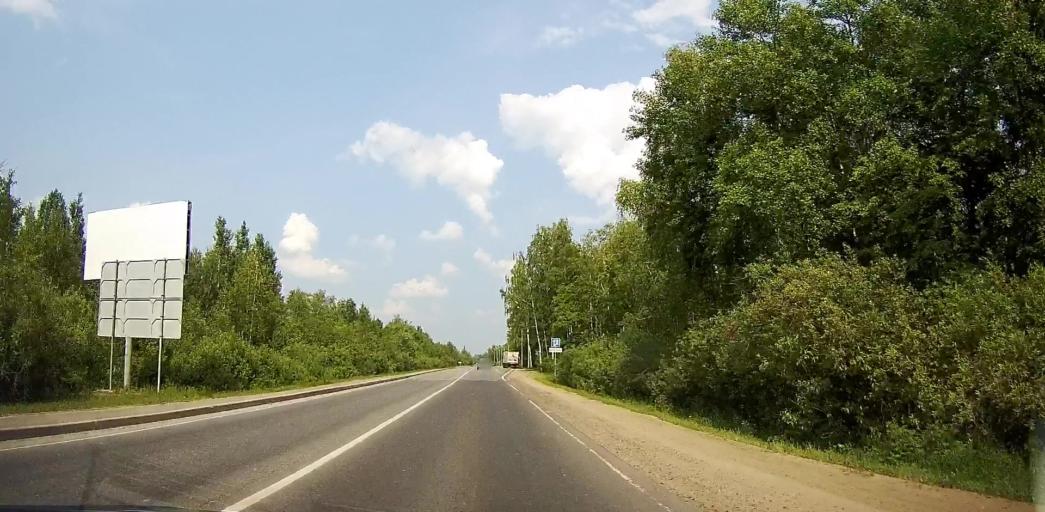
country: RU
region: Moskovskaya
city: Stupino
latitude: 54.9082
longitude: 38.0910
